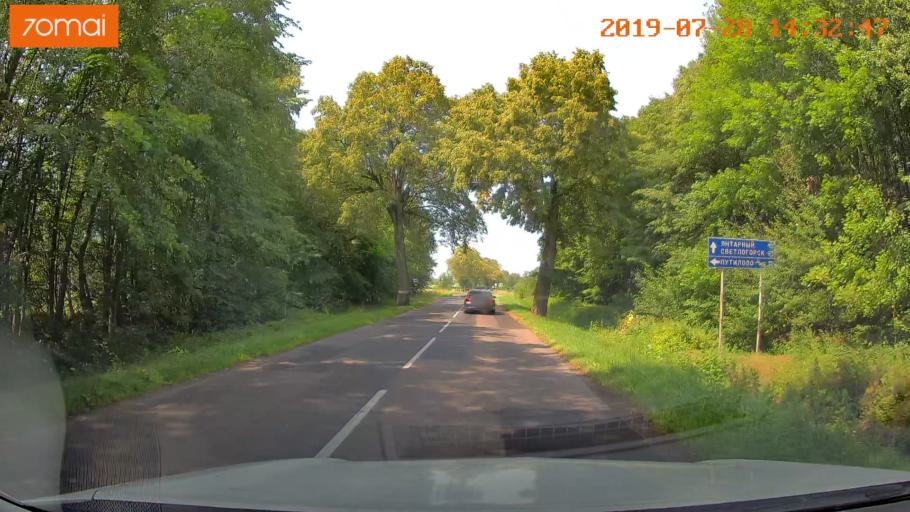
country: RU
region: Kaliningrad
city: Primorsk
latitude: 54.8150
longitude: 20.0381
